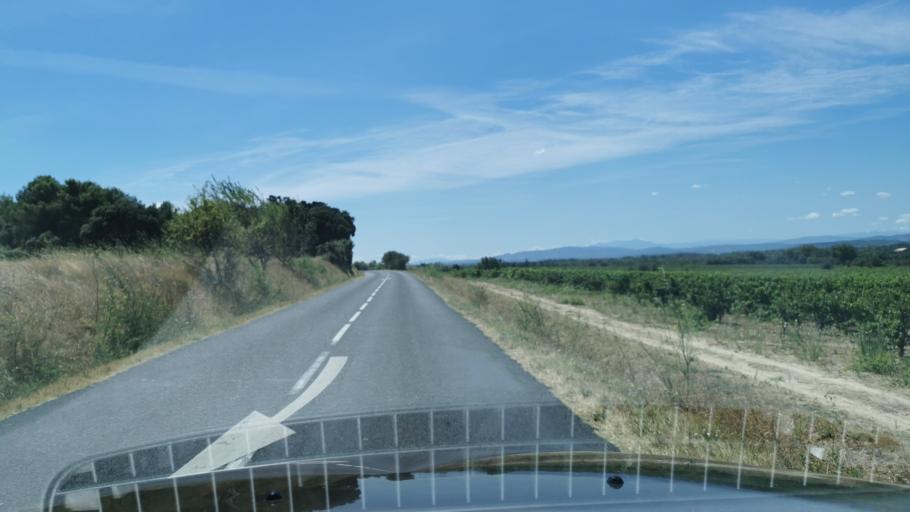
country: FR
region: Languedoc-Roussillon
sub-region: Departement de l'Aude
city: Vinassan
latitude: 43.1817
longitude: 3.0630
